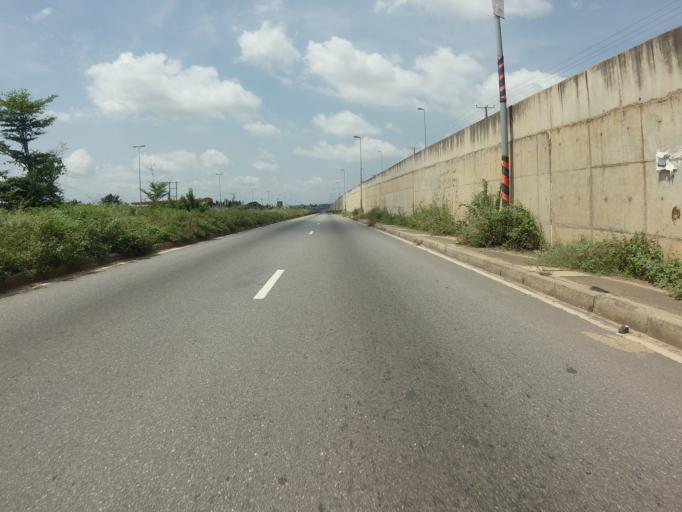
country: GH
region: Greater Accra
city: Gbawe
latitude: 5.6240
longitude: -0.3033
